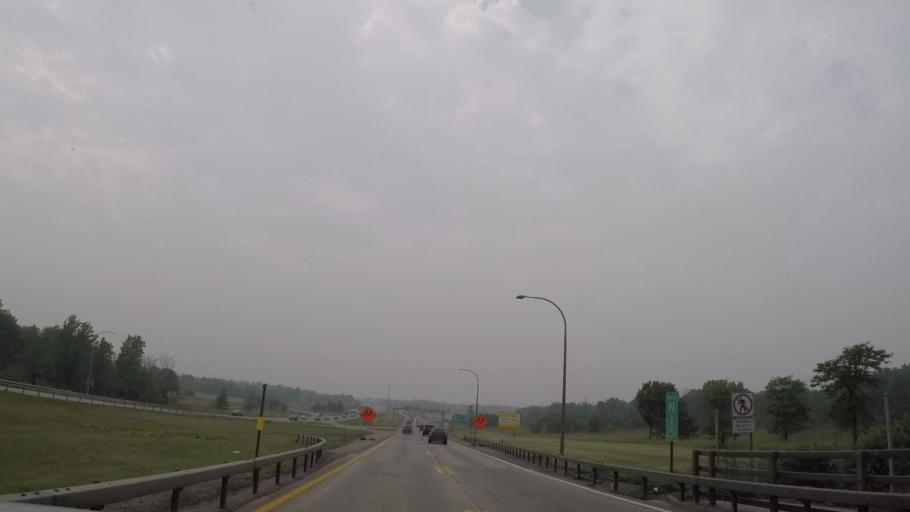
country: US
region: New York
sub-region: Erie County
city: Grandyle Village
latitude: 43.0012
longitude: -78.9411
